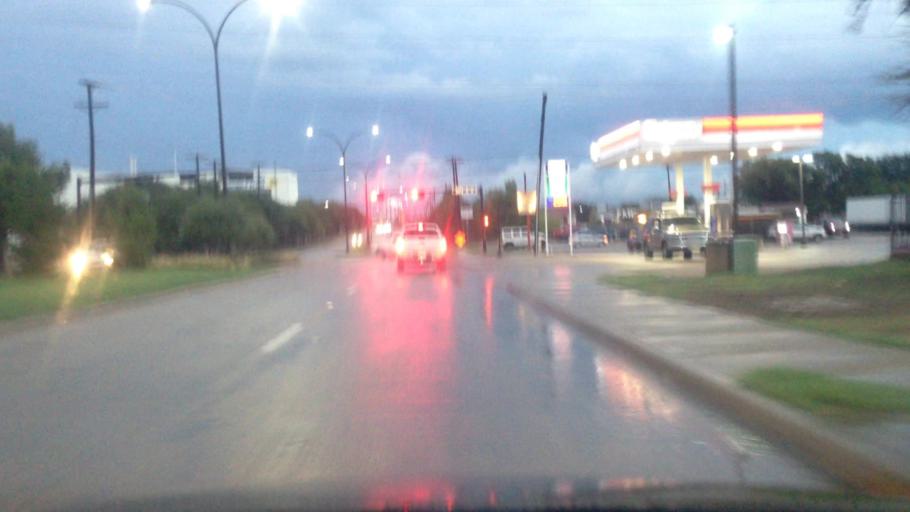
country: US
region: Texas
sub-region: Tarrant County
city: Arlington
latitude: 32.7352
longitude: -97.0724
